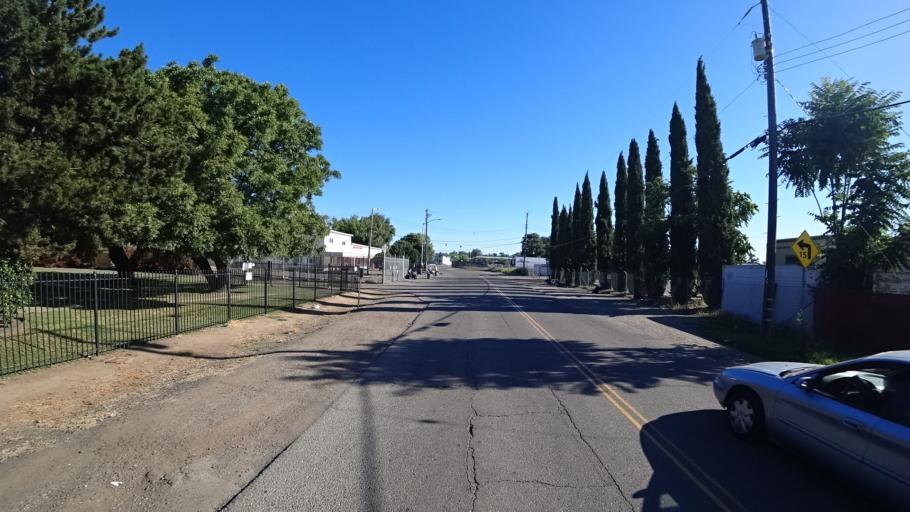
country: US
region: California
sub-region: Sacramento County
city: Sacramento
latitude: 38.5946
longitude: -121.4973
